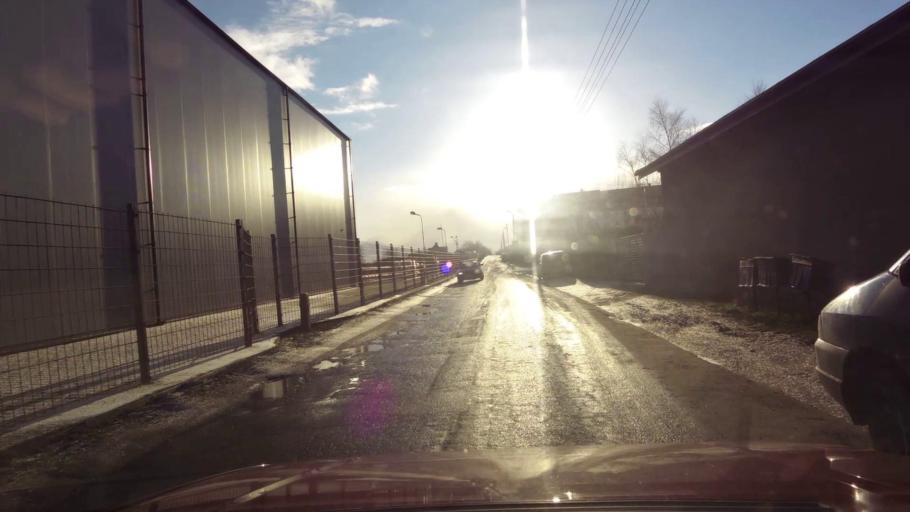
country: PL
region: West Pomeranian Voivodeship
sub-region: Koszalin
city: Koszalin
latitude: 54.1647
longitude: 16.1830
